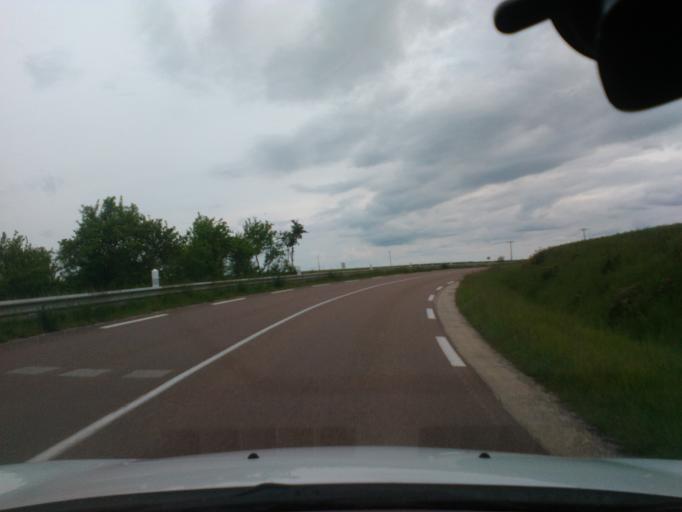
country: FR
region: Champagne-Ardenne
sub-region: Departement de l'Aube
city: Bar-sur-Aube
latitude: 48.2221
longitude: 4.8140
